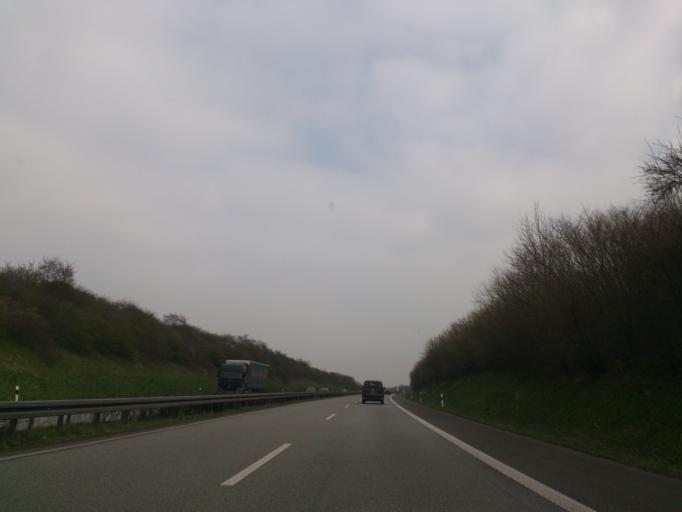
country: DE
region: North Rhine-Westphalia
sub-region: Regierungsbezirk Dusseldorf
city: Bruggen
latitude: 51.2060
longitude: 6.1655
